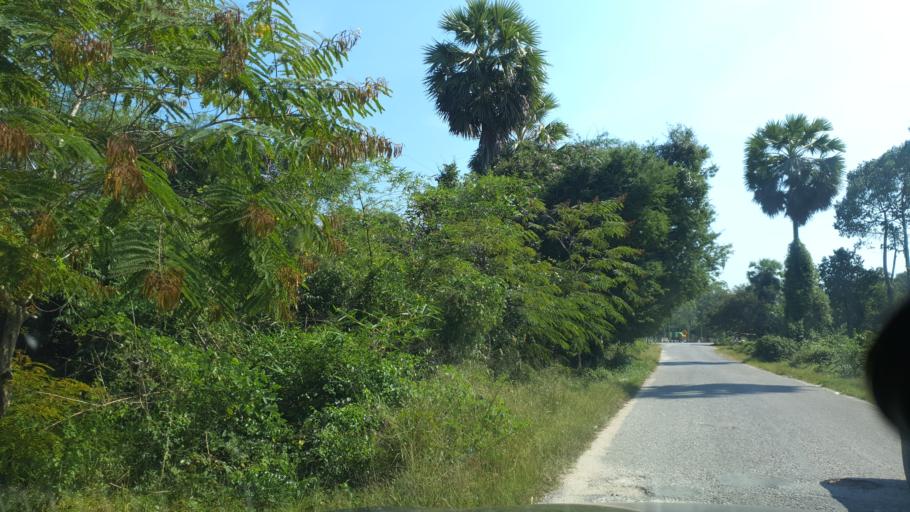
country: TH
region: Surat Thani
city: Tha Chana
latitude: 9.5883
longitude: 99.2014
